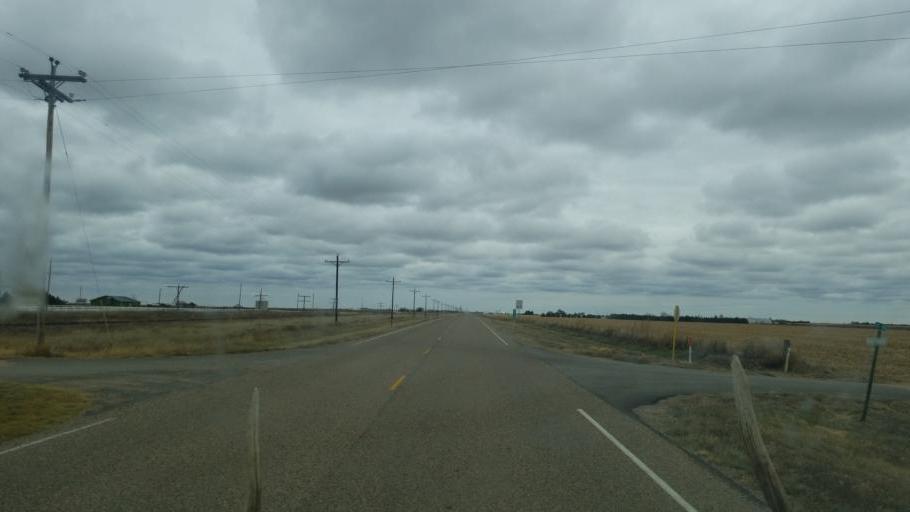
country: US
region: Colorado
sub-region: Kiowa County
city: Eads
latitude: 38.4842
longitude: -102.8411
